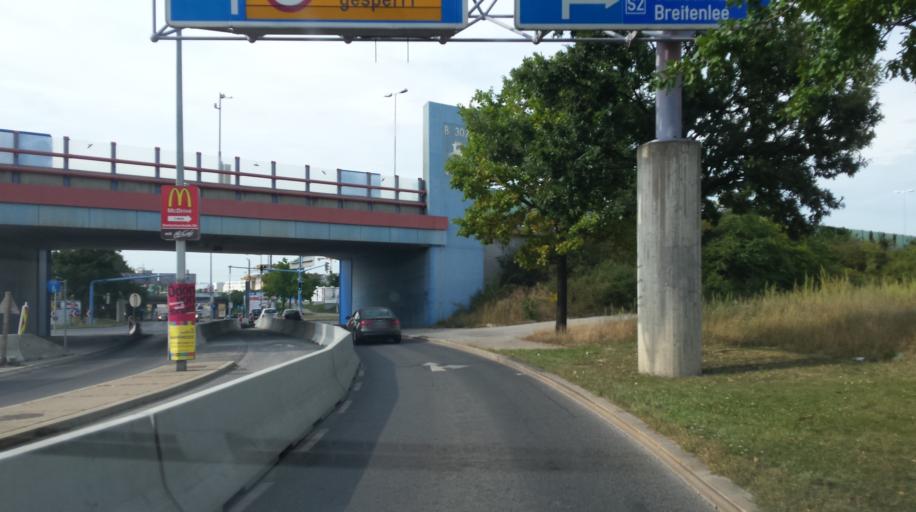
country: AT
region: Lower Austria
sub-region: Politischer Bezirk Wien-Umgebung
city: Gerasdorf bei Wien
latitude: 48.2402
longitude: 16.4607
